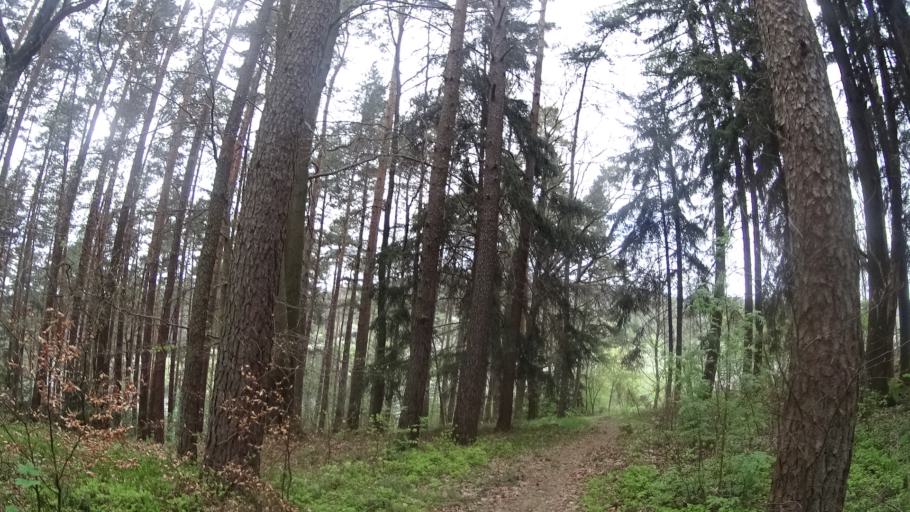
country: DE
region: Bavaria
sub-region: Upper Franconia
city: Kleinsendelbach
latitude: 49.6199
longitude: 11.1819
